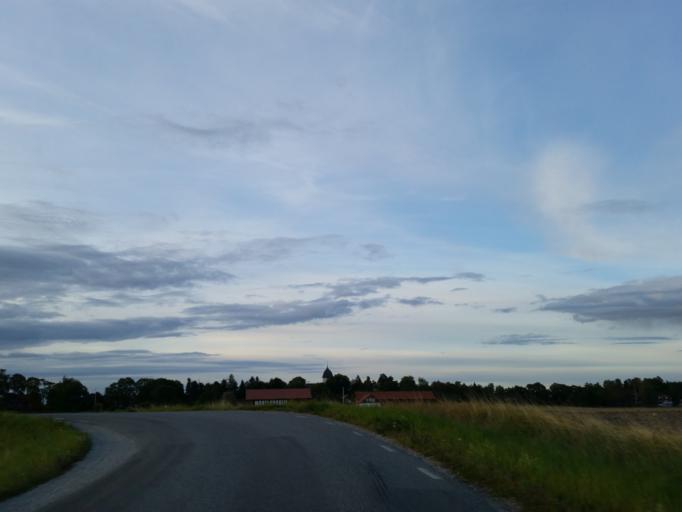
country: SE
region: Stockholm
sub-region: Sigtuna Kommun
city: Marsta
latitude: 59.6353
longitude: 17.8814
